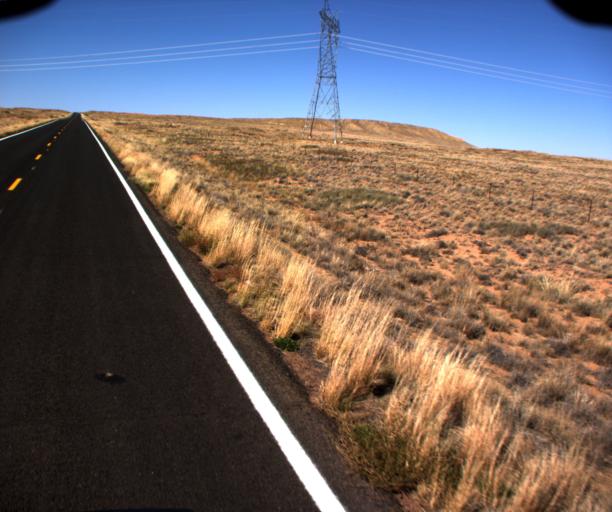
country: US
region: Arizona
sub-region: Coconino County
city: Tuba City
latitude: 35.9510
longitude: -110.9227
